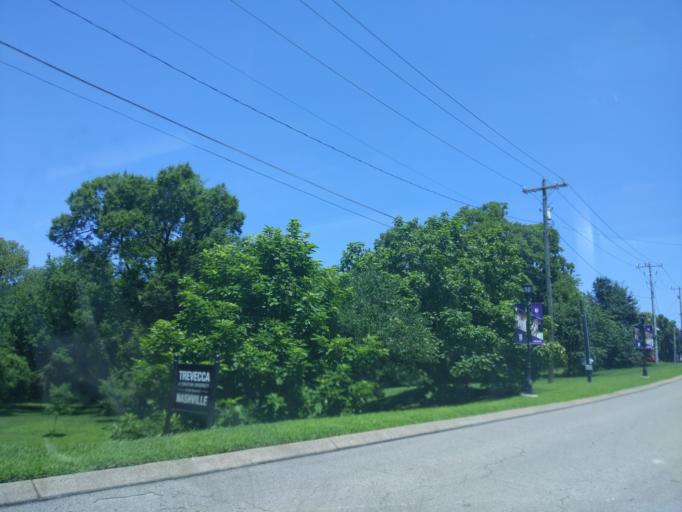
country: US
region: Tennessee
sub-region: Davidson County
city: Nashville
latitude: 36.1391
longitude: -86.7533
